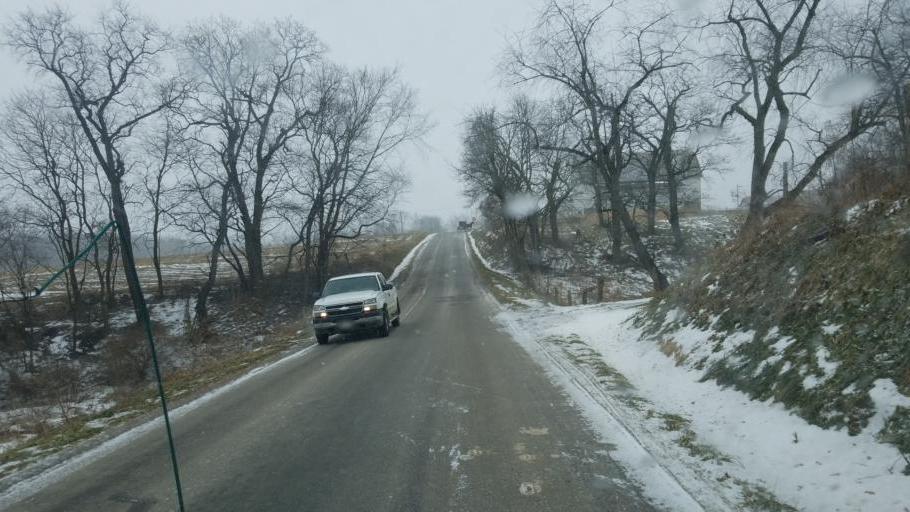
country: US
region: Ohio
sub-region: Wayne County
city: Apple Creek
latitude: 40.6765
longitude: -81.8422
